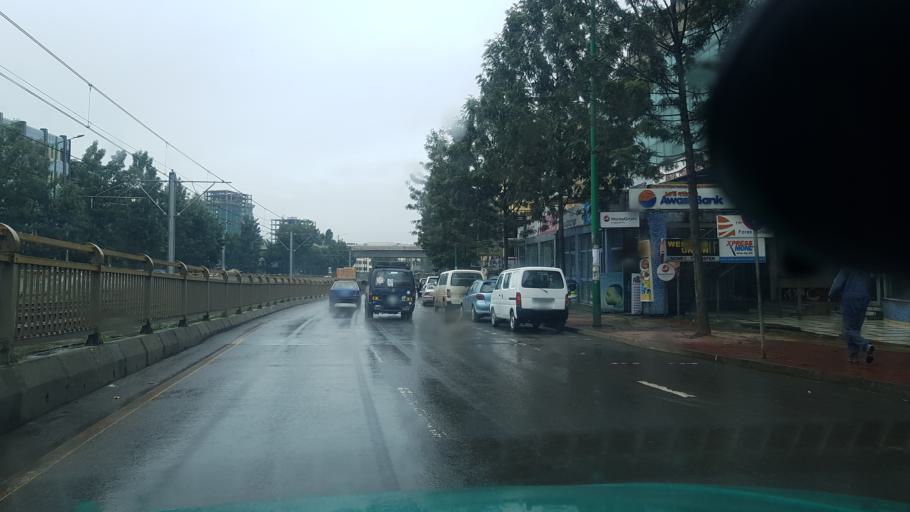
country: ET
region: Adis Abeba
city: Addis Ababa
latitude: 8.9976
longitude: 38.7591
